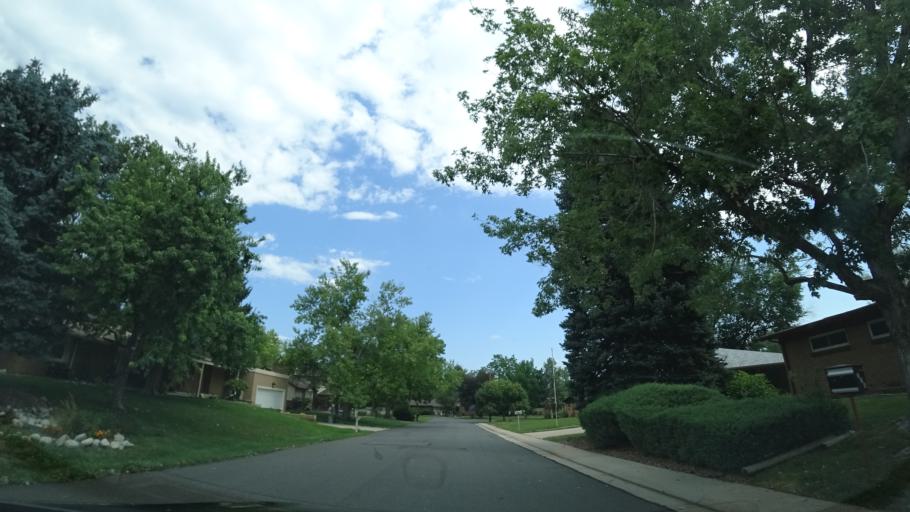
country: US
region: Colorado
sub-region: Jefferson County
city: Lakewood
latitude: 39.7213
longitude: -105.0757
